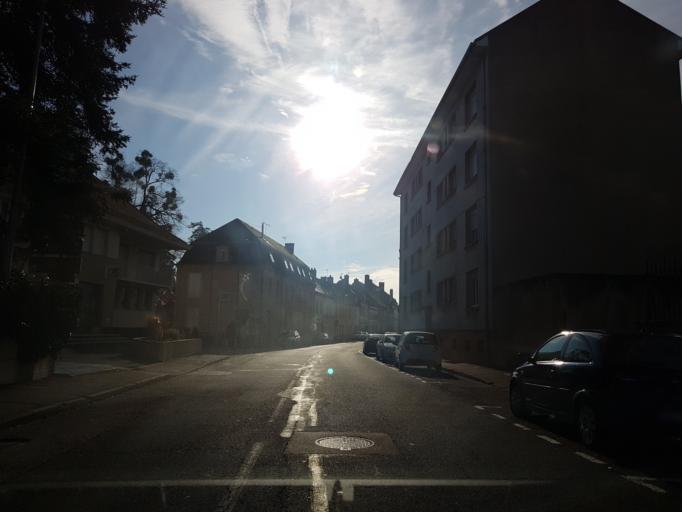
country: FR
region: Bourgogne
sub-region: Departement de Saone-et-Loire
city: Bourbon-Lancy
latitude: 46.6226
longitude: 3.7733
